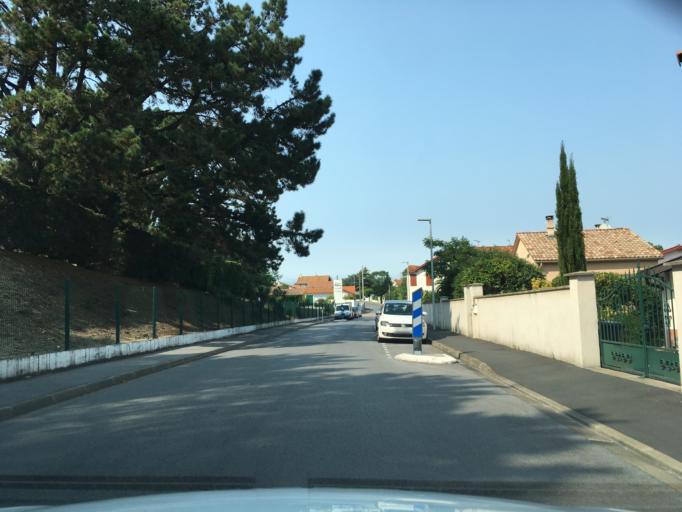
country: FR
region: Aquitaine
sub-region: Departement des Pyrenees-Atlantiques
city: Bayonne
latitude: 43.5075
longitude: -1.5023
